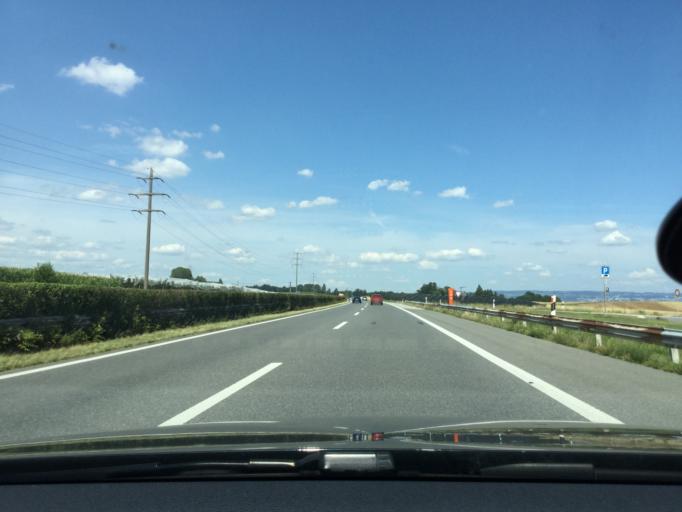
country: CH
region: Vaud
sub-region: Morges District
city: Saint-Prex
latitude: 46.4815
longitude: 6.4350
